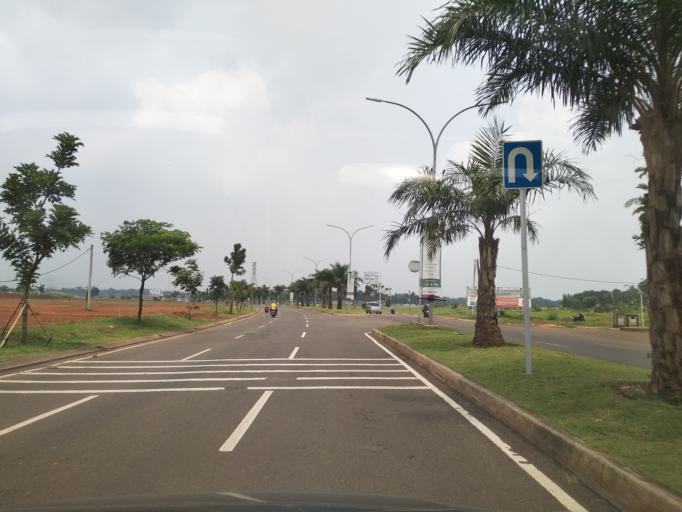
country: ID
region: West Java
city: Bekasi
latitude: -6.2963
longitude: 107.0427
